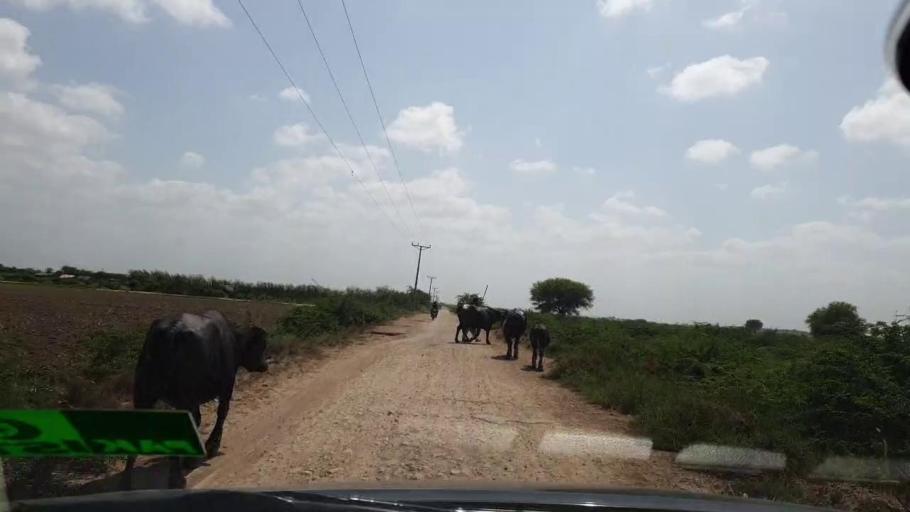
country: PK
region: Sindh
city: Kadhan
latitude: 24.6113
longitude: 69.1853
